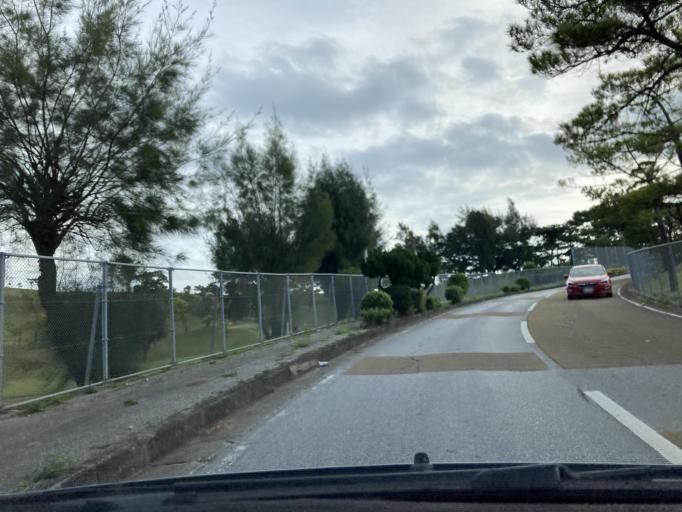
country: JP
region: Okinawa
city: Ginowan
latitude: 26.2161
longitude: 127.7456
